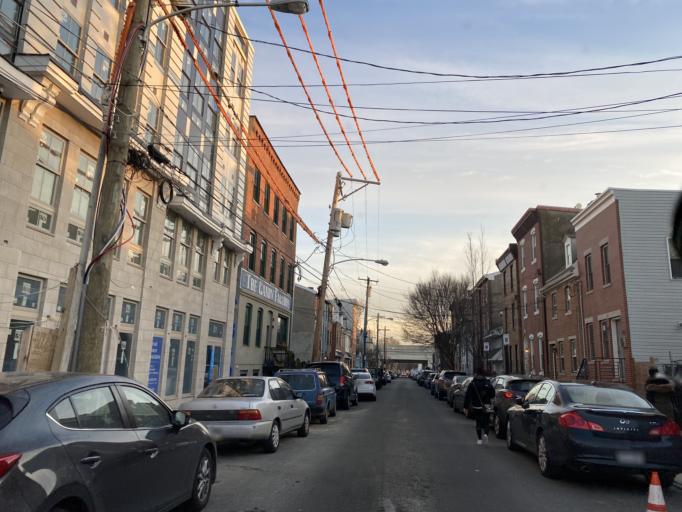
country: US
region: Pennsylvania
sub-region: Philadelphia County
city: Philadelphia
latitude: 39.9700
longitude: -75.1303
